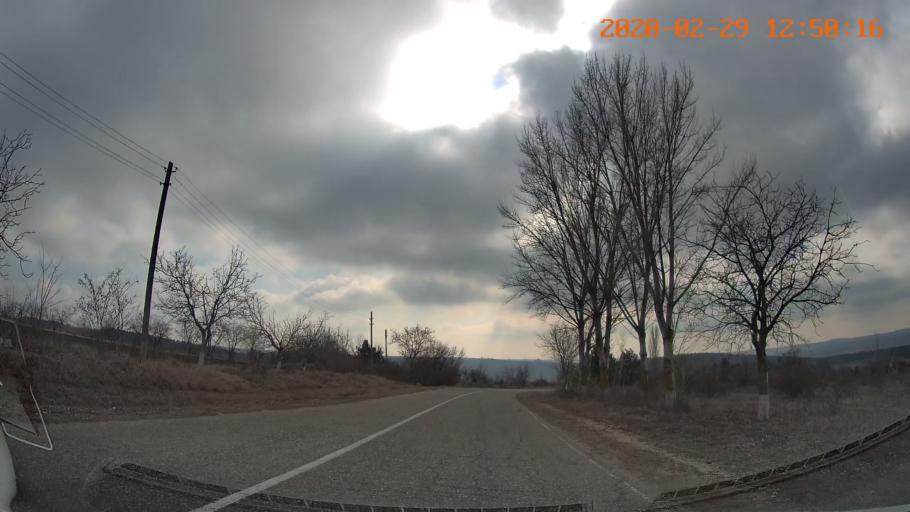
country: MD
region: Telenesti
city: Camenca
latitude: 48.1256
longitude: 28.7407
